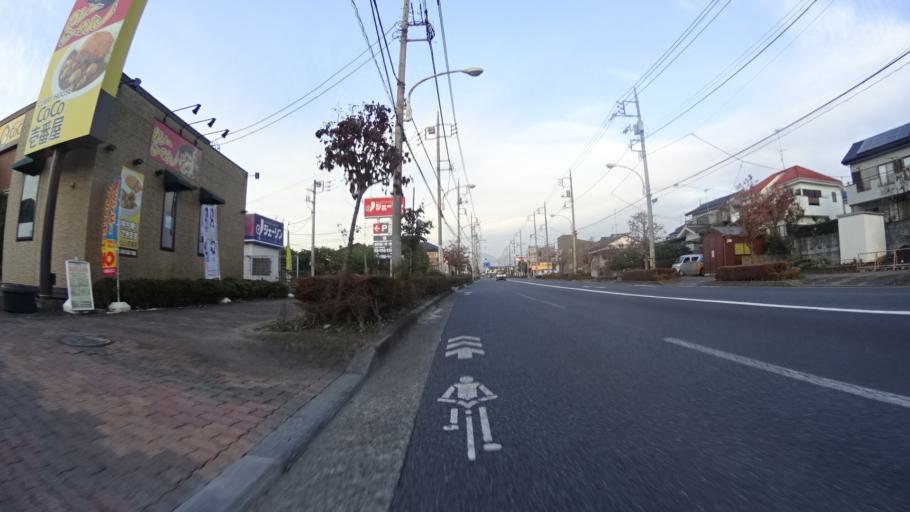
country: JP
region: Tokyo
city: Fussa
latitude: 35.7222
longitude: 139.3071
